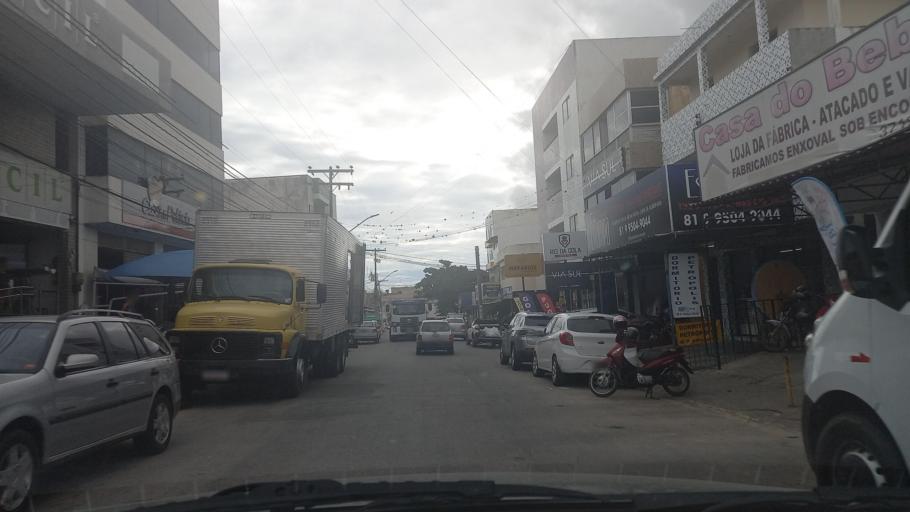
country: BR
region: Pernambuco
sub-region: Caruaru
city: Caruaru
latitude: -8.2934
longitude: -35.9745
